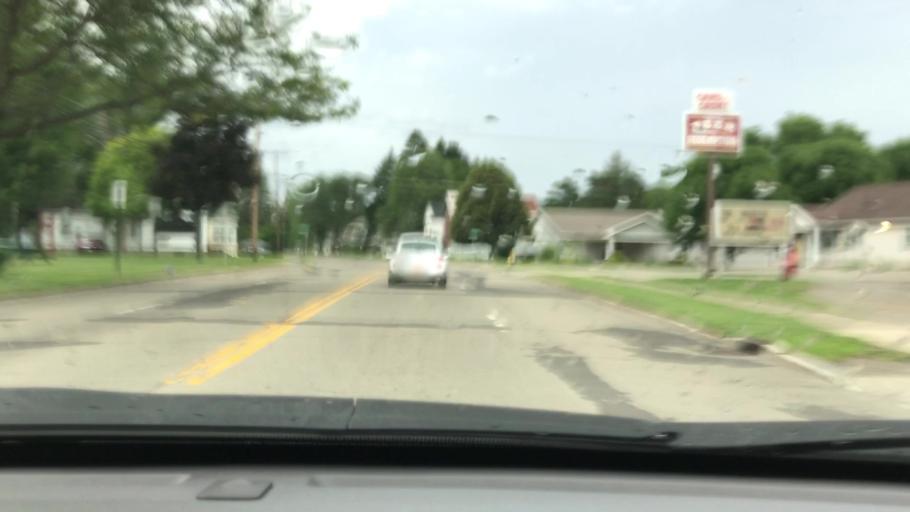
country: US
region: New York
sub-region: Cattaraugus County
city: Salamanca
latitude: 42.1661
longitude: -78.6946
